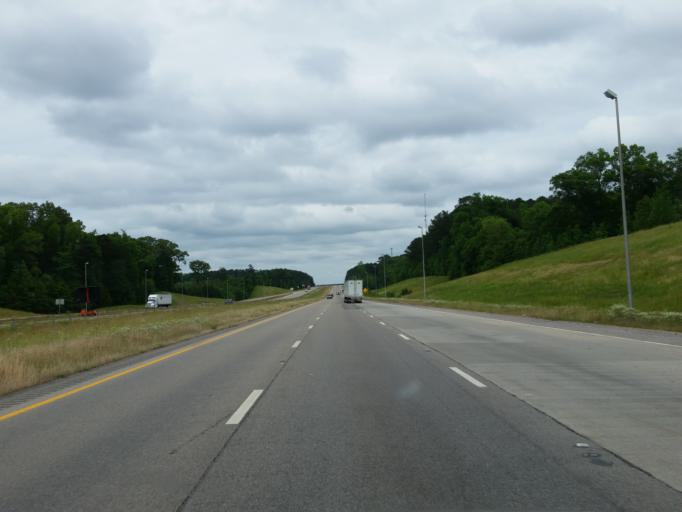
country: US
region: Alabama
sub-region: Sumter County
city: York
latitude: 32.4409
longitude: -88.4290
